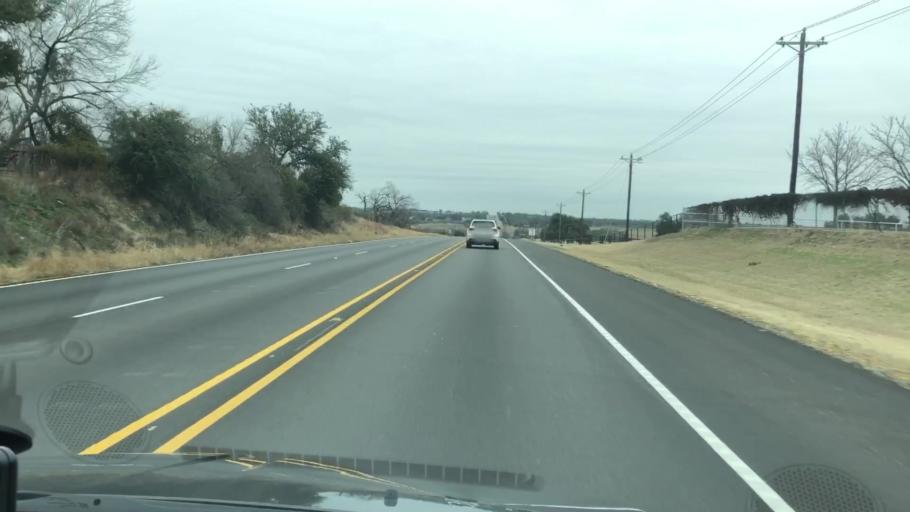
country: US
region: Texas
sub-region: Erath County
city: Stephenville
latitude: 32.3092
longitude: -98.1850
